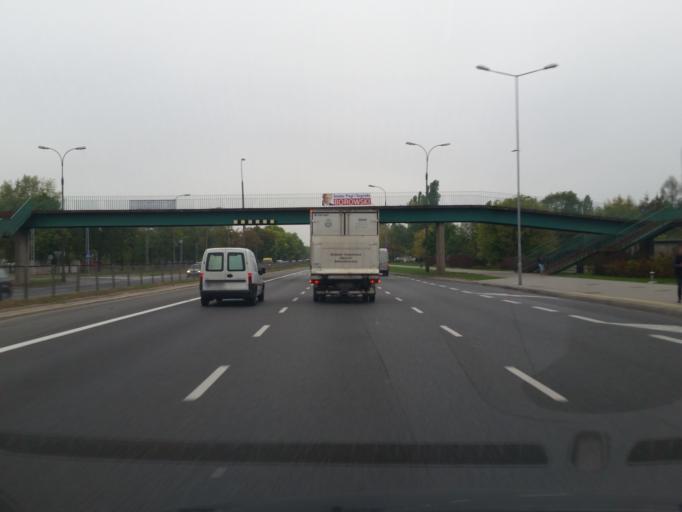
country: PL
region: Masovian Voivodeship
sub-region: Warszawa
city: Zoliborz
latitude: 52.2782
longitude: 21.0123
